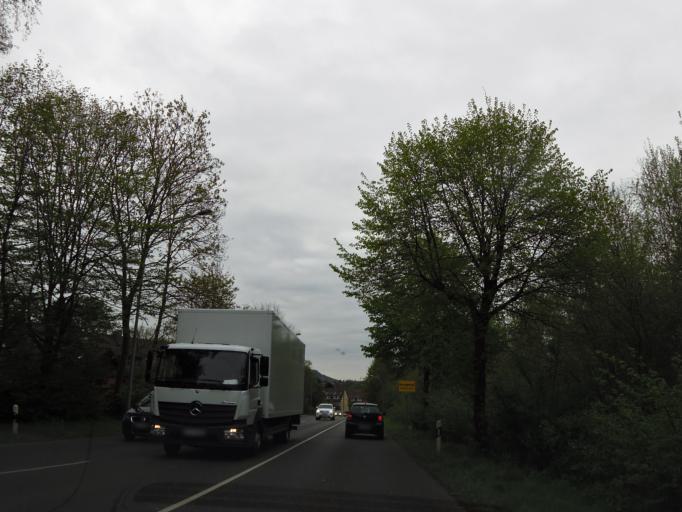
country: DE
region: North Rhine-Westphalia
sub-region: Regierungsbezirk Koln
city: Herzogenrath
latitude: 50.8637
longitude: 6.0854
